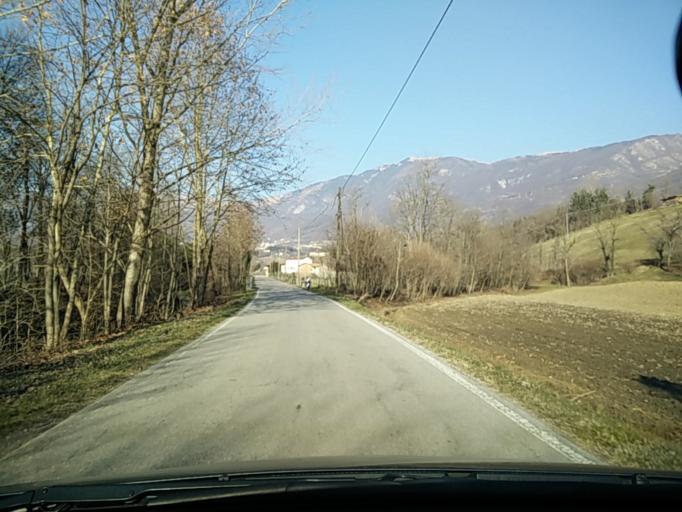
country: IT
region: Veneto
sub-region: Provincia di Treviso
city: Sarmede
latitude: 45.9834
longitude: 12.3751
